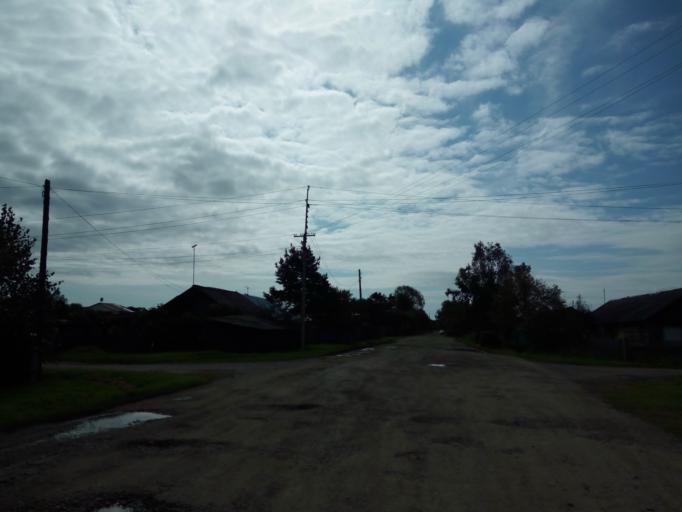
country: RU
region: Primorskiy
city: Dal'nerechensk
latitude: 45.9178
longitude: 133.7228
